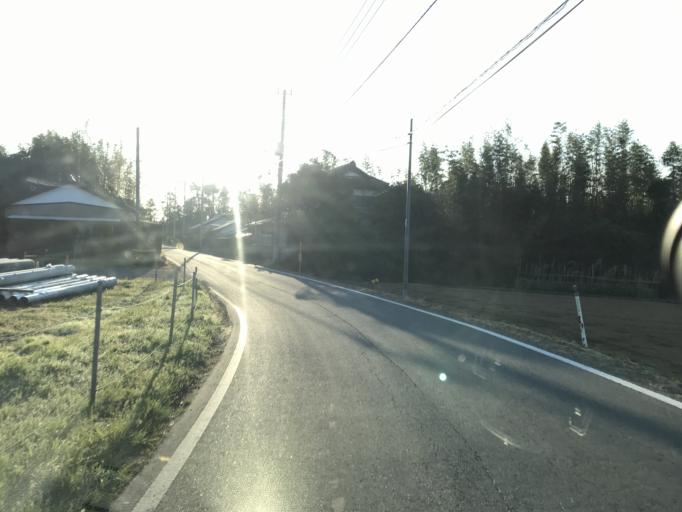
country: JP
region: Chiba
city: Yokaichiba
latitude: 35.7606
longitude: 140.5573
